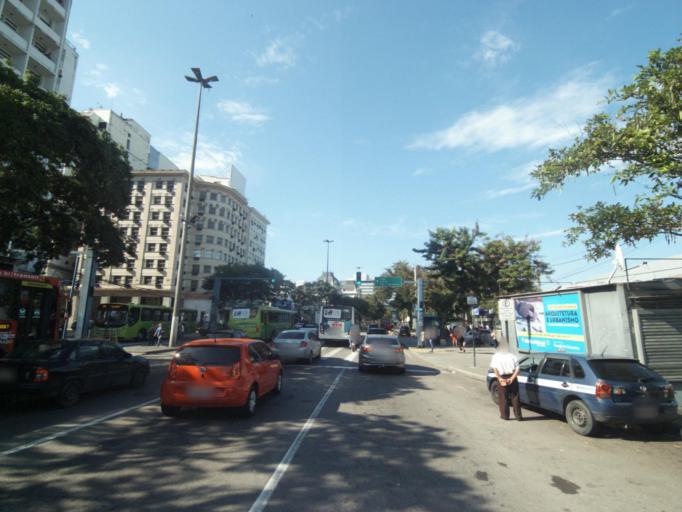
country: BR
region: Rio de Janeiro
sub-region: Niteroi
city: Niteroi
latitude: -22.8930
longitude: -43.1238
